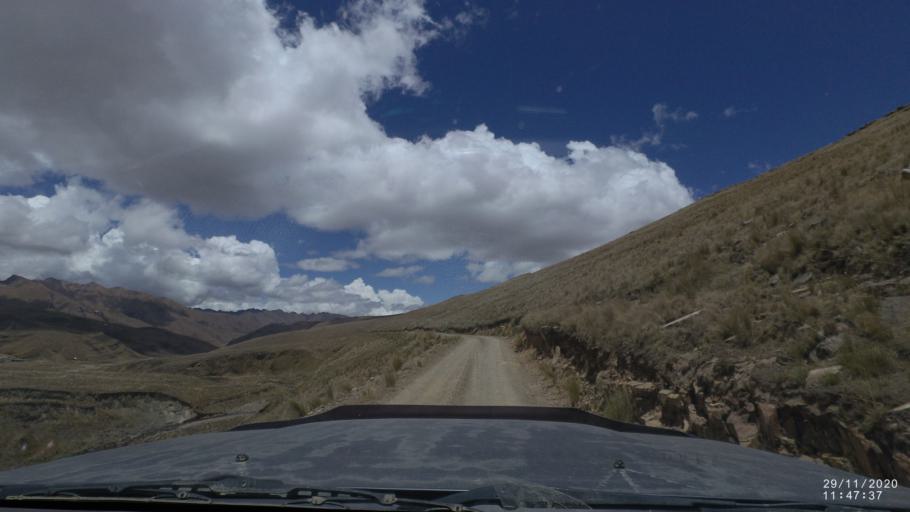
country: BO
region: Cochabamba
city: Cochabamba
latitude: -17.1828
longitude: -66.2529
